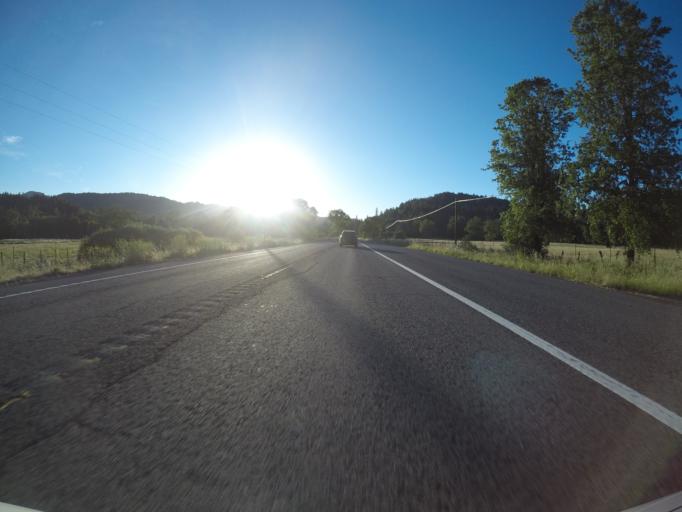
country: US
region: California
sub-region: Mendocino County
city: Laytonville
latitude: 39.7448
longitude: -123.5223
